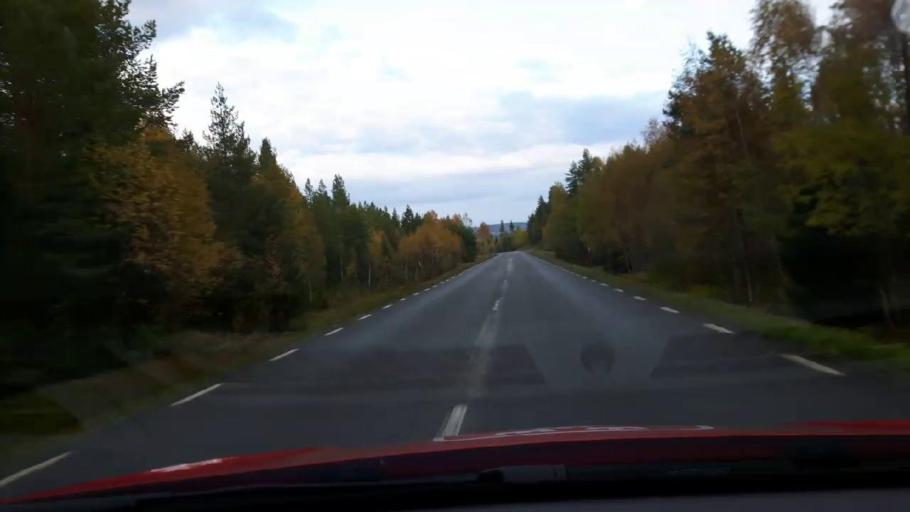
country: SE
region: Jaemtland
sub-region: OEstersunds Kommun
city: Ostersund
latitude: 63.3213
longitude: 14.6416
